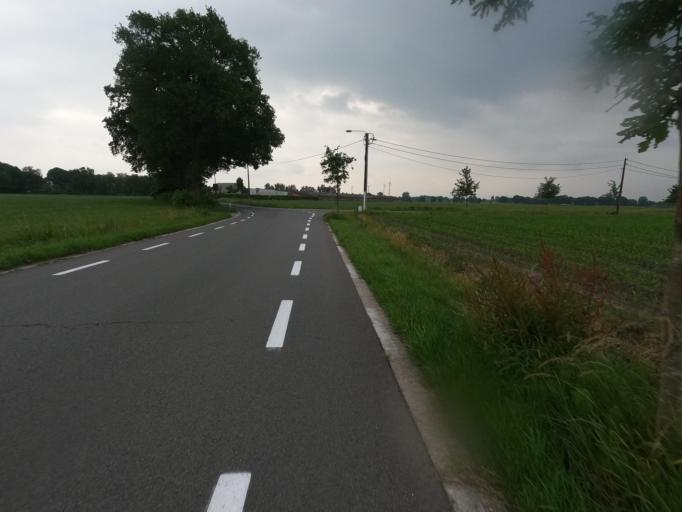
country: BE
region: Flanders
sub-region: Provincie Antwerpen
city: Essen
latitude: 51.4630
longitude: 4.4964
